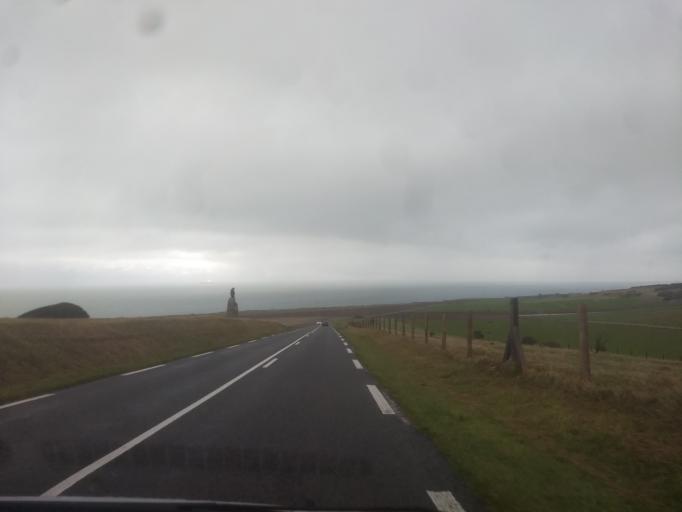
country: FR
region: Nord-Pas-de-Calais
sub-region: Departement du Pas-de-Calais
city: Sangatte
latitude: 50.9296
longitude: 1.7209
